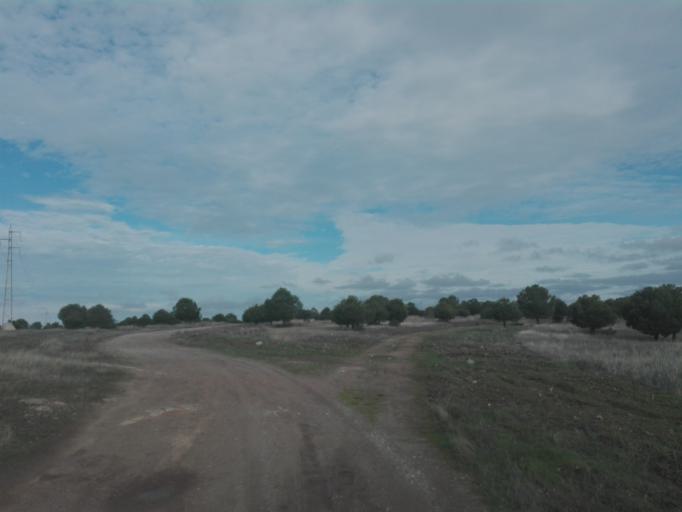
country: ES
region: Extremadura
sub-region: Provincia de Badajoz
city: Villagarcia de la Torre
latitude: 38.3166
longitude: -6.0845
